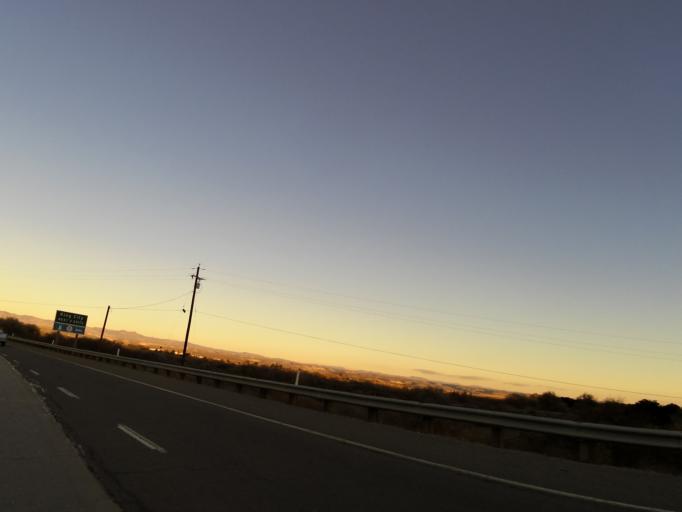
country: US
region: California
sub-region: Monterey County
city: King City
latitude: 36.1983
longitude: -121.1450
